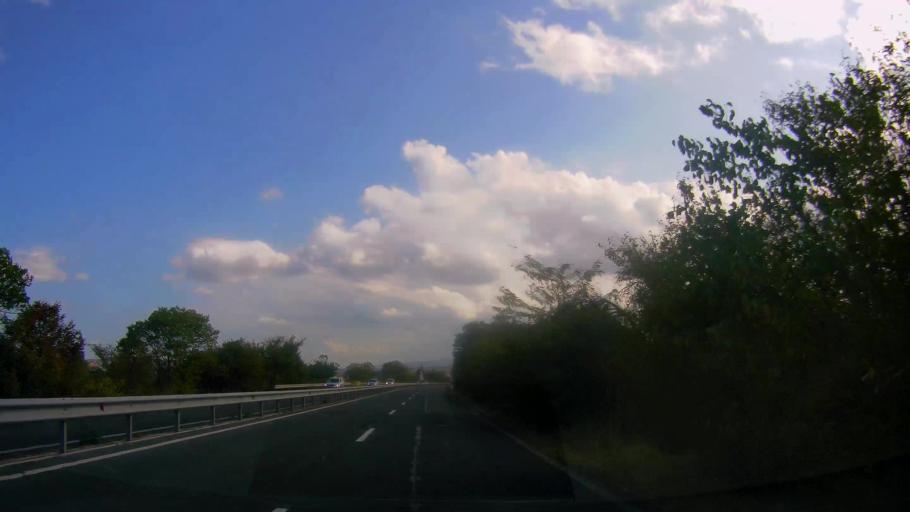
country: BG
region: Burgas
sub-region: Obshtina Sozopol
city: Chernomorets
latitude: 42.4313
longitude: 27.6388
